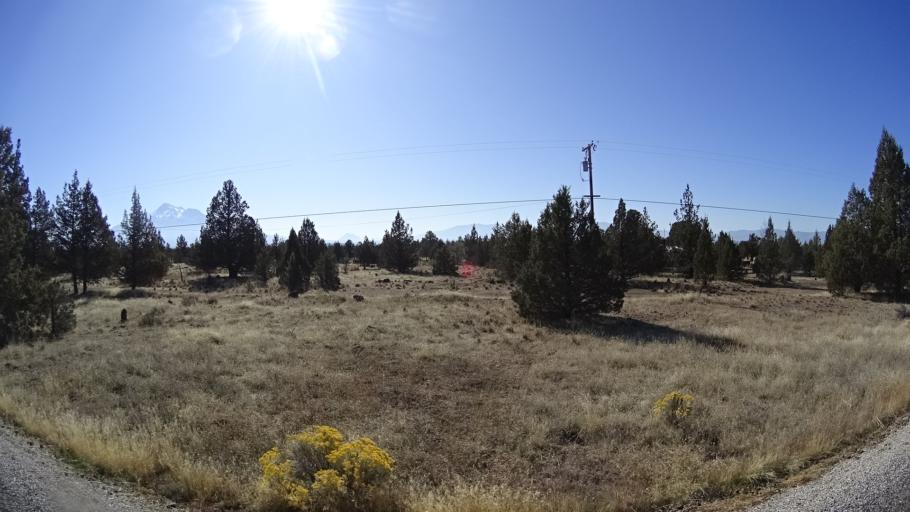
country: US
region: California
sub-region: Siskiyou County
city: Montague
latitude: 41.6596
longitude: -122.3789
